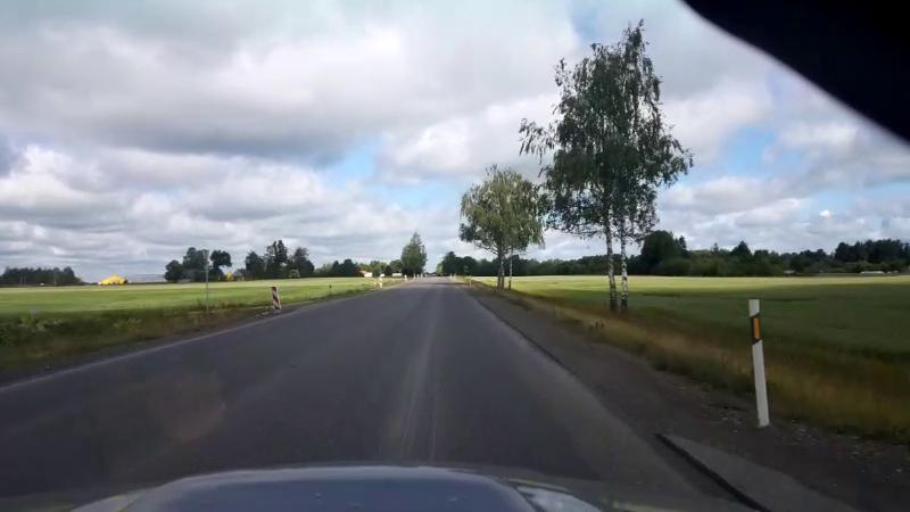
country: LV
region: Bauskas Rajons
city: Bauska
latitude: 56.3175
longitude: 24.3247
